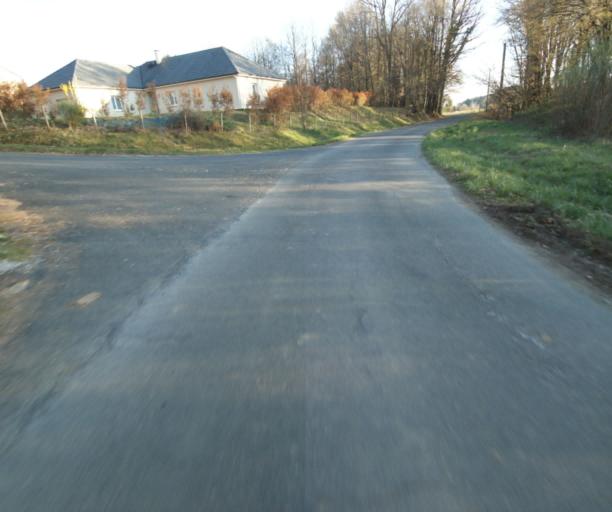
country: FR
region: Limousin
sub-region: Departement de la Correze
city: Seilhac
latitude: 45.3552
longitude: 1.7059
